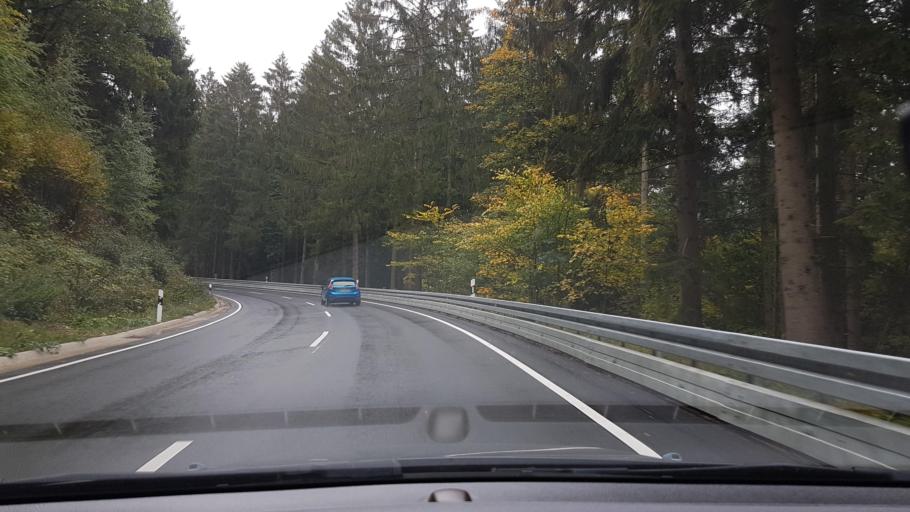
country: DE
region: Lower Saxony
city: Bad Grund
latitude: 51.8237
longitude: 10.2243
